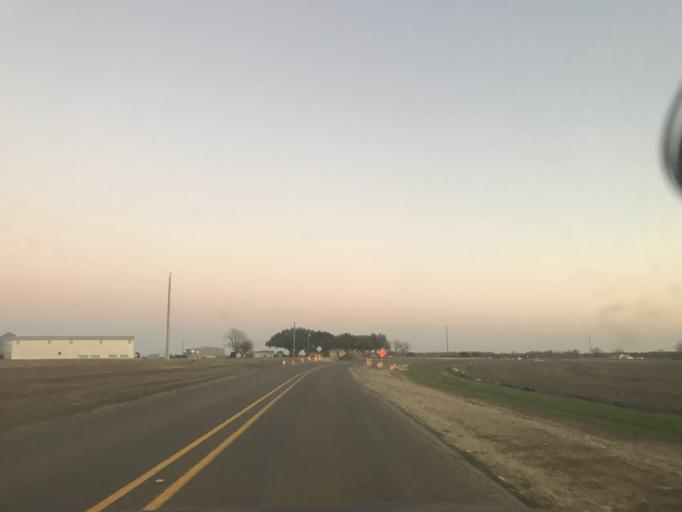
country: US
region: Texas
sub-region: Williamson County
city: Hutto
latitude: 30.4932
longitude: -97.4926
